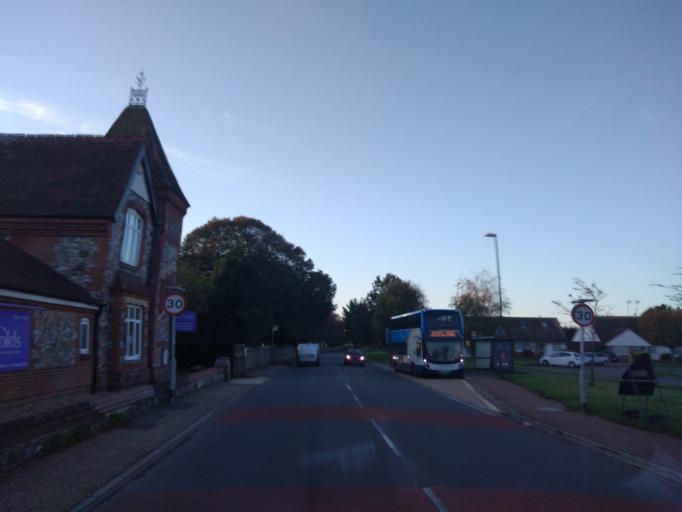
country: GB
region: England
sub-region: West Sussex
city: Littlehampton
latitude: 50.8193
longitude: -0.5284
